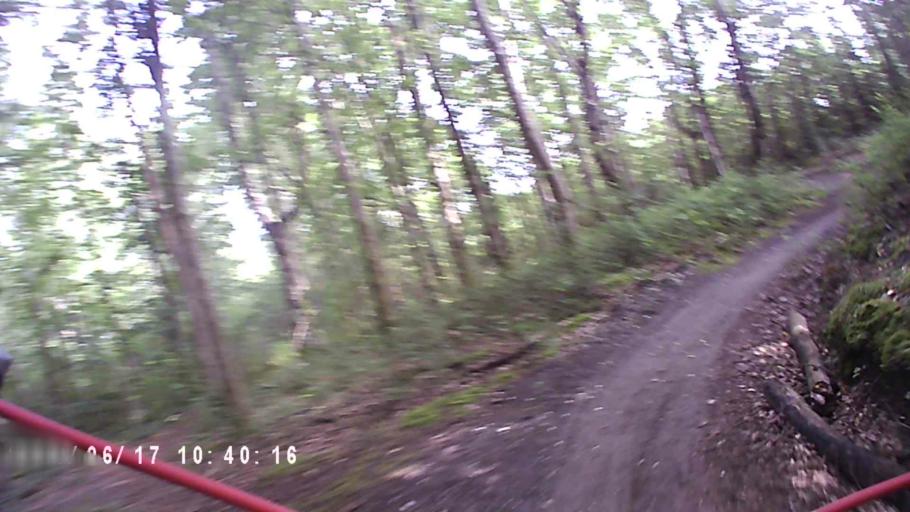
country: NL
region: Friesland
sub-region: Gemeente Dongeradeel
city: Anjum
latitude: 53.4034
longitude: 6.2312
